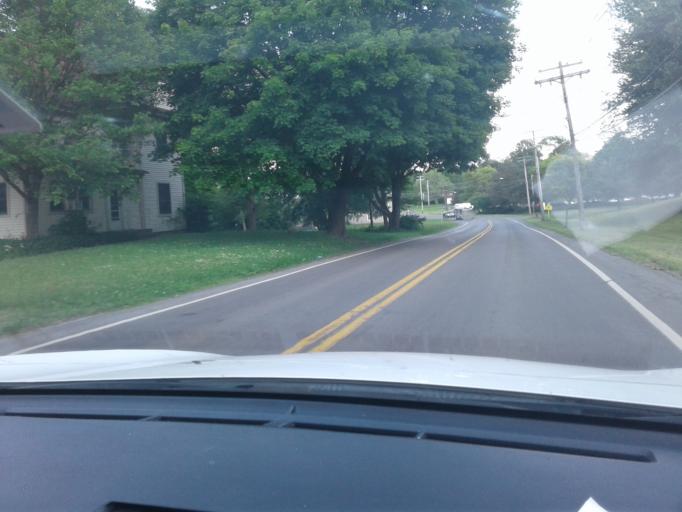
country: US
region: New York
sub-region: Onondaga County
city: East Syracuse
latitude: 43.0455
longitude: -76.0738
